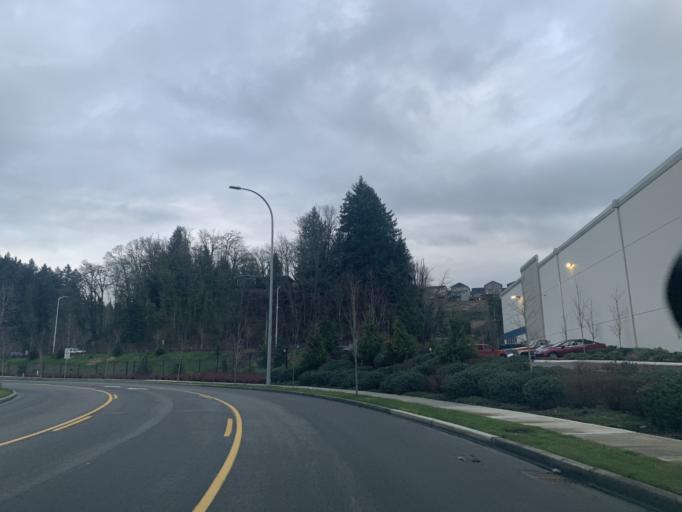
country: US
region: Washington
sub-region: Pierce County
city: Milton
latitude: 47.2335
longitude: -122.3254
